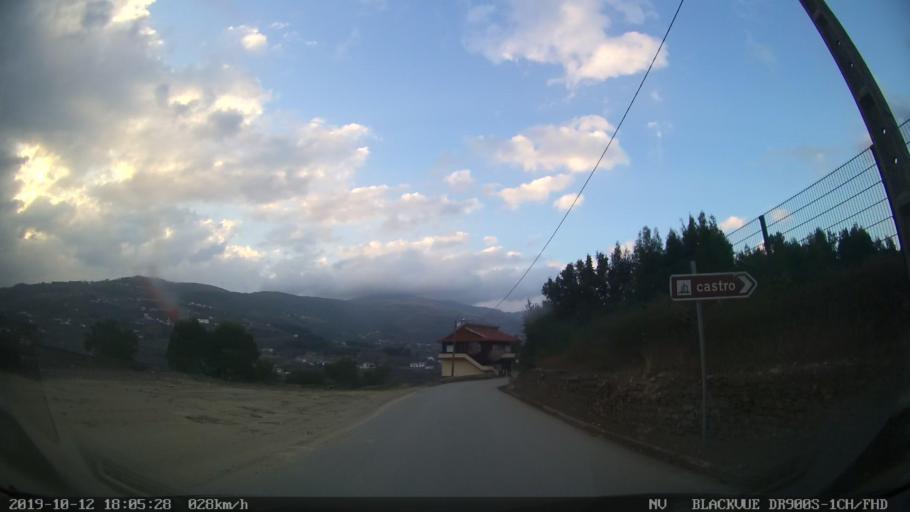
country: PT
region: Vila Real
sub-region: Mesao Frio
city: Mesao Frio
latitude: 41.1769
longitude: -7.8450
